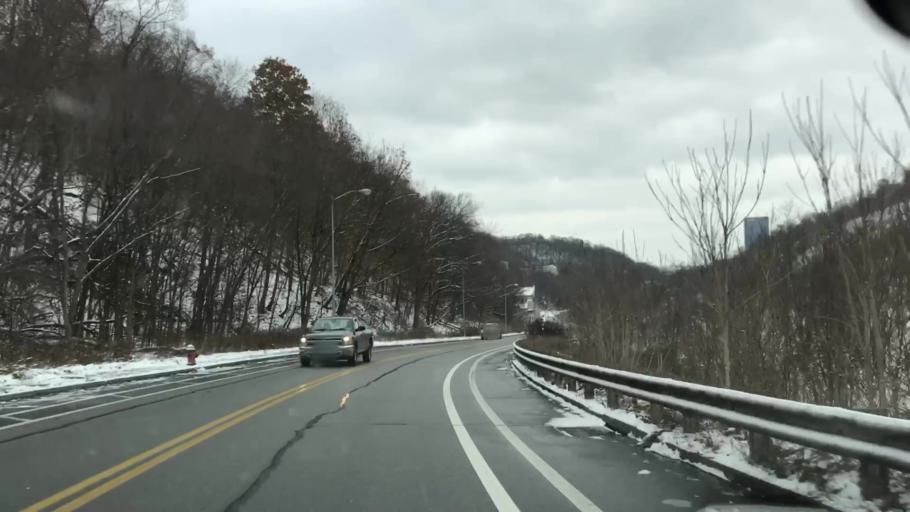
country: US
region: Pennsylvania
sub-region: Allegheny County
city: Millvale
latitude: 40.4708
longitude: -80.0026
